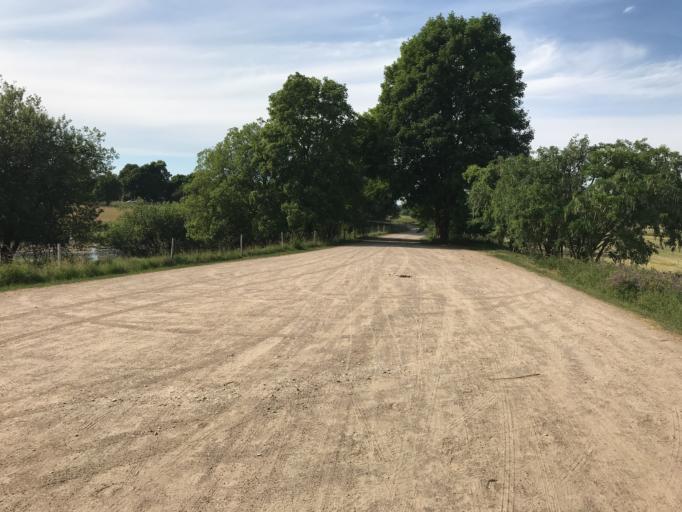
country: DK
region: Capital Region
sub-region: Fureso Kommune
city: Vaerlose
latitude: 55.7620
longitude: 12.3530
